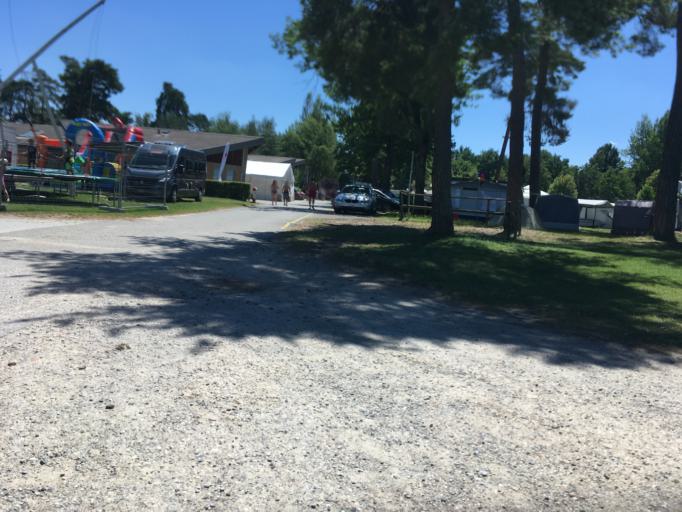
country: CH
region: Vaud
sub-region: Broye-Vully District
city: Avenches
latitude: 46.9055
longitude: 7.0487
